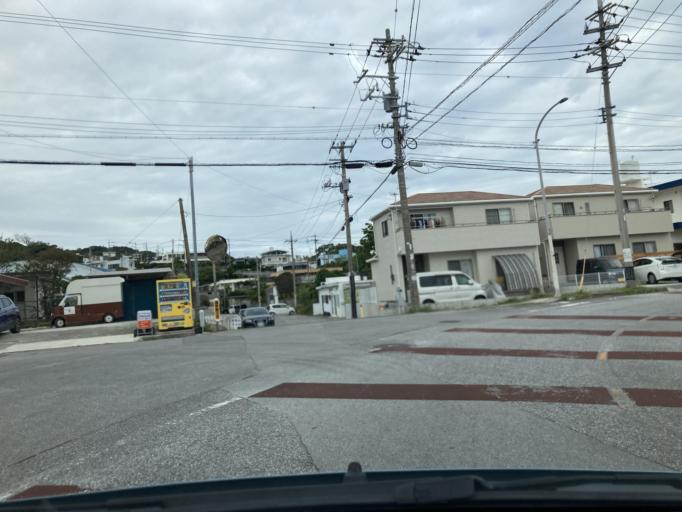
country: JP
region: Okinawa
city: Tomigusuku
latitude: 26.1413
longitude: 127.7916
